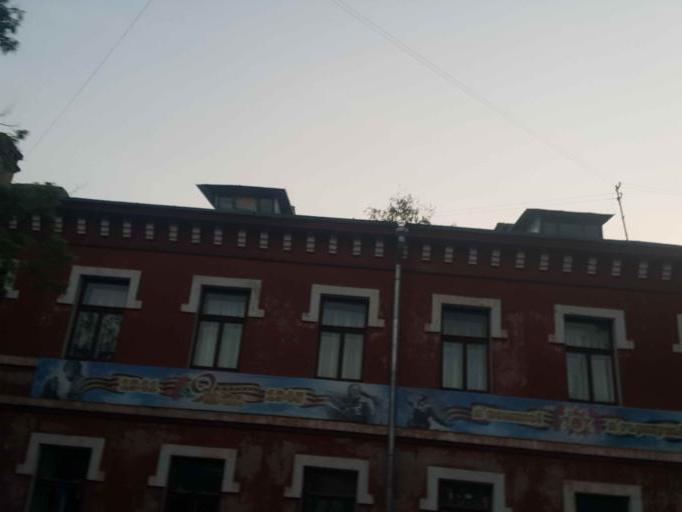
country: RU
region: Tambov
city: Kotovsk
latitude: 52.5895
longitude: 41.4976
